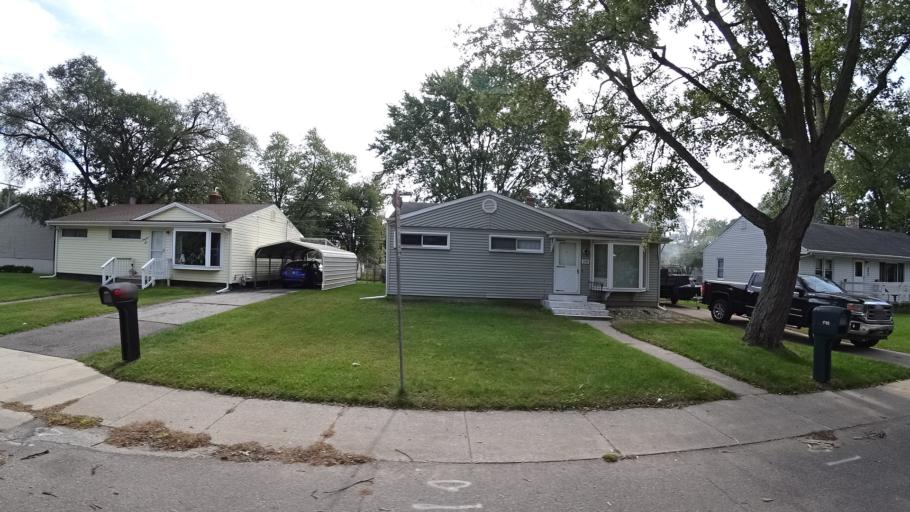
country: US
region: Indiana
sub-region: LaPorte County
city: Trail Creek
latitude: 41.7168
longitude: -86.8656
